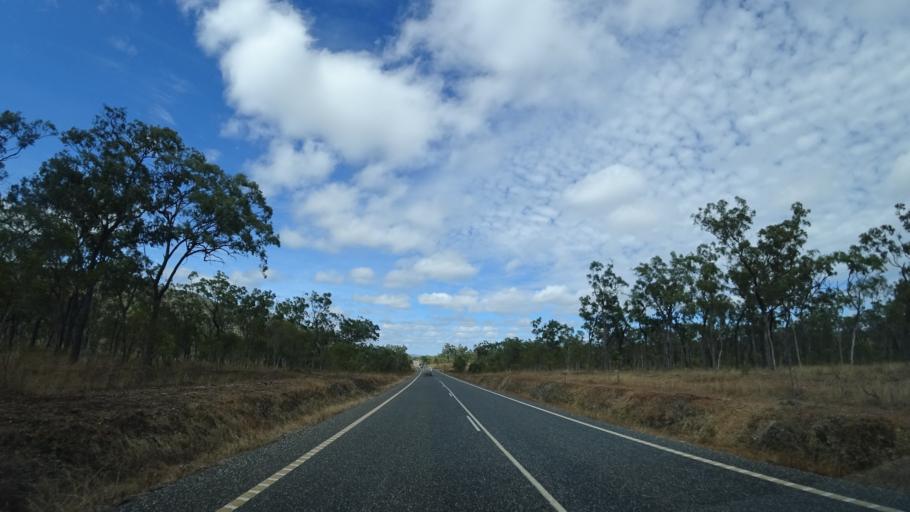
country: AU
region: Queensland
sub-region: Cairns
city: Port Douglas
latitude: -16.3187
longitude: 144.7187
